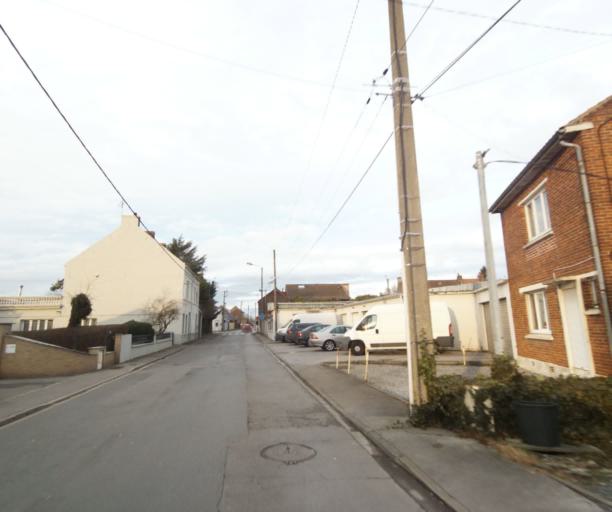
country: FR
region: Nord-Pas-de-Calais
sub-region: Departement du Nord
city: Conde-sur-l'Escaut
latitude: 50.4706
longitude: 3.5982
